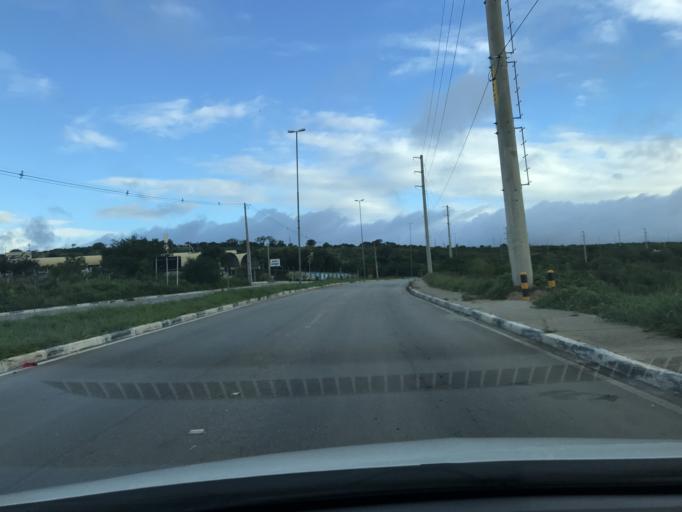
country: BR
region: Pernambuco
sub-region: Caruaru
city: Caruaru
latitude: -8.3023
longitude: -35.9401
